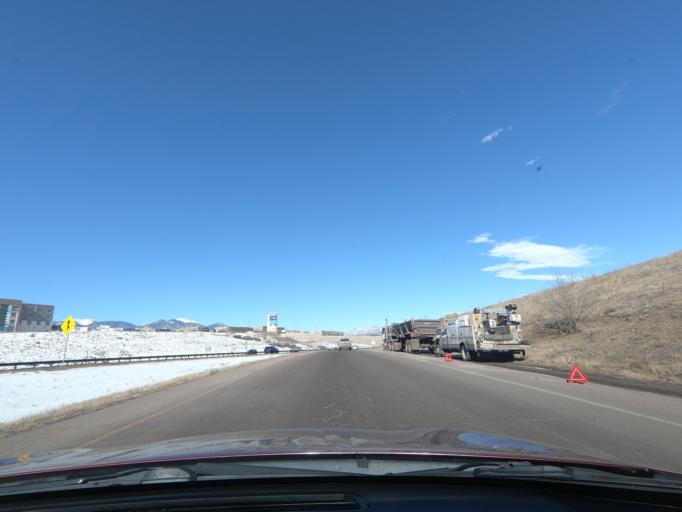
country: US
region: Colorado
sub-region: El Paso County
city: Stratmoor
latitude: 38.7677
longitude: -104.7774
